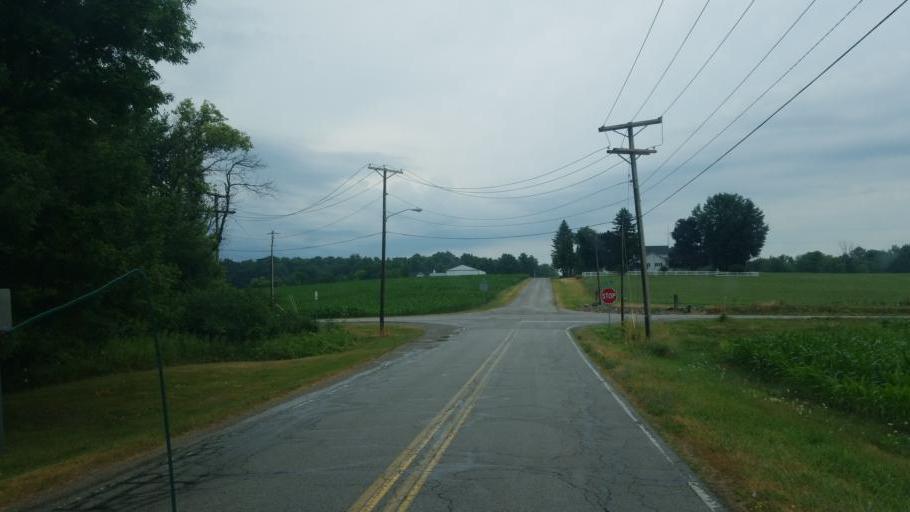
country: US
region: Indiana
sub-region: Steuben County
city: Hamilton
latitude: 41.5289
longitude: -84.9314
